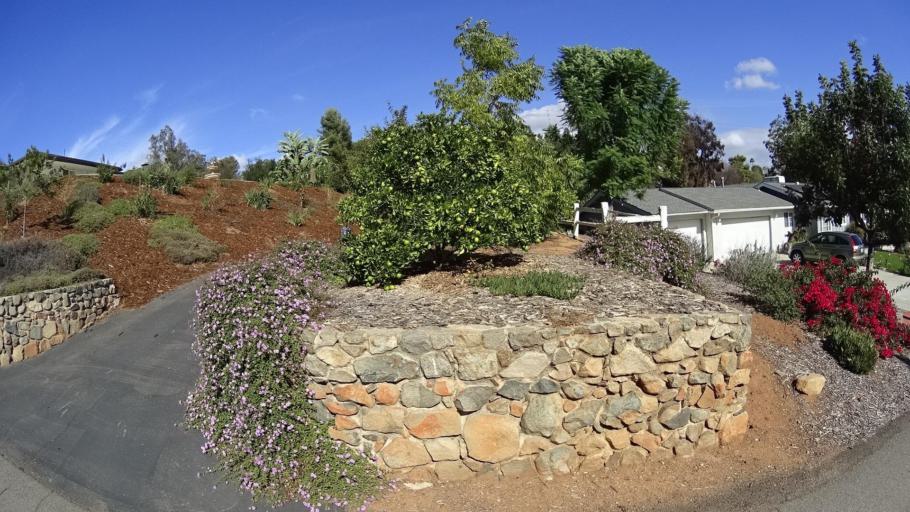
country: US
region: California
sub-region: San Diego County
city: Casa de Oro-Mount Helix
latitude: 32.7646
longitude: -116.9551
